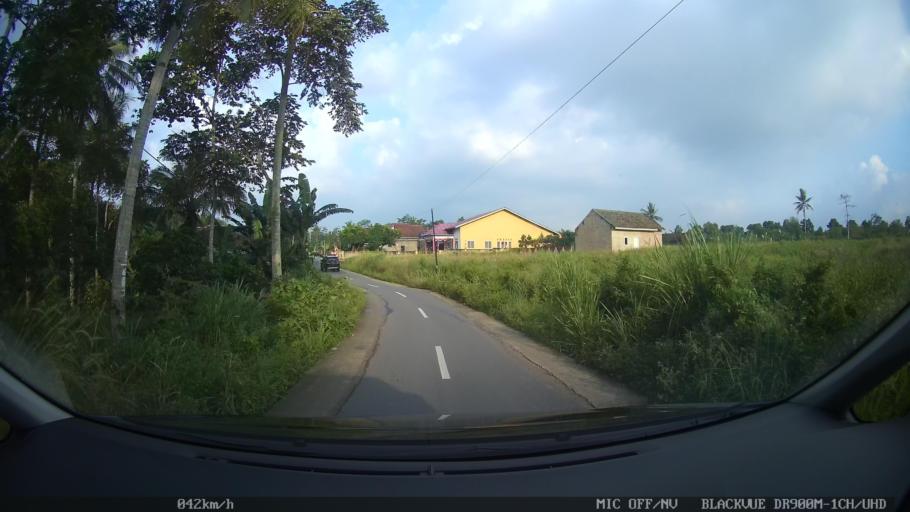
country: ID
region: Lampung
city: Panjang
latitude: -5.3930
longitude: 105.3496
